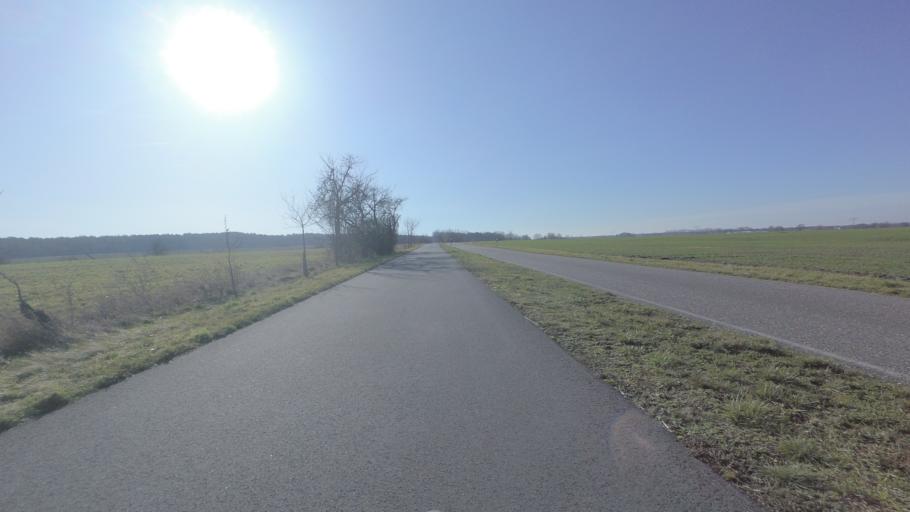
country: DE
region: Brandenburg
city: Luckenwalde
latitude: 52.0379
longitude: 13.1354
